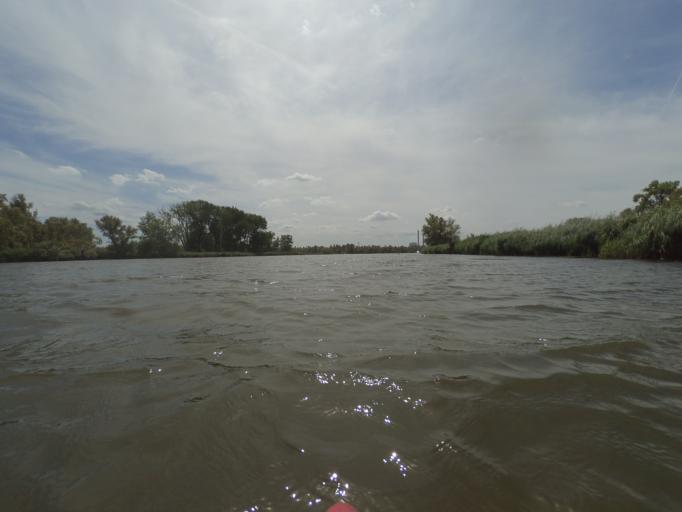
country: NL
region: North Brabant
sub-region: Gemeente Geertruidenberg
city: Geertruidenberg
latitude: 51.7301
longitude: 4.8466
